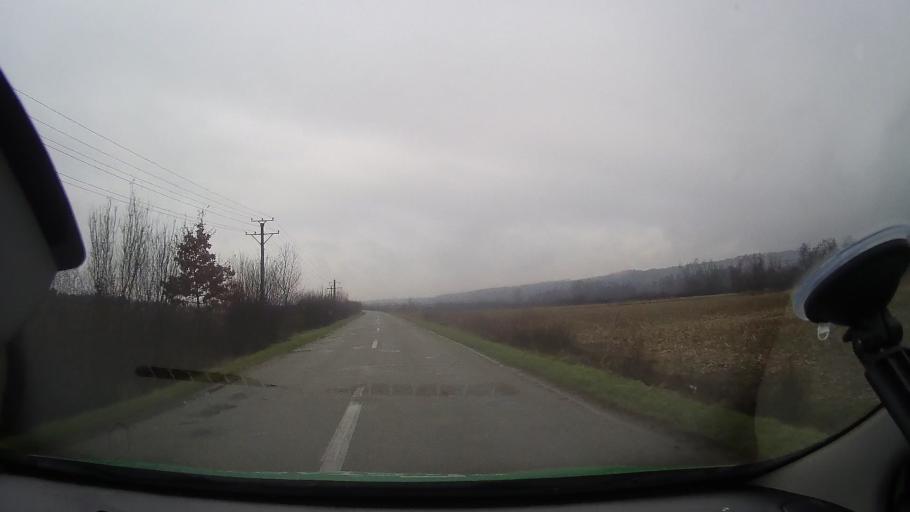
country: RO
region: Arad
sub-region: Comuna Ignesti
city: Ignesti
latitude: 46.4051
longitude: 22.2082
